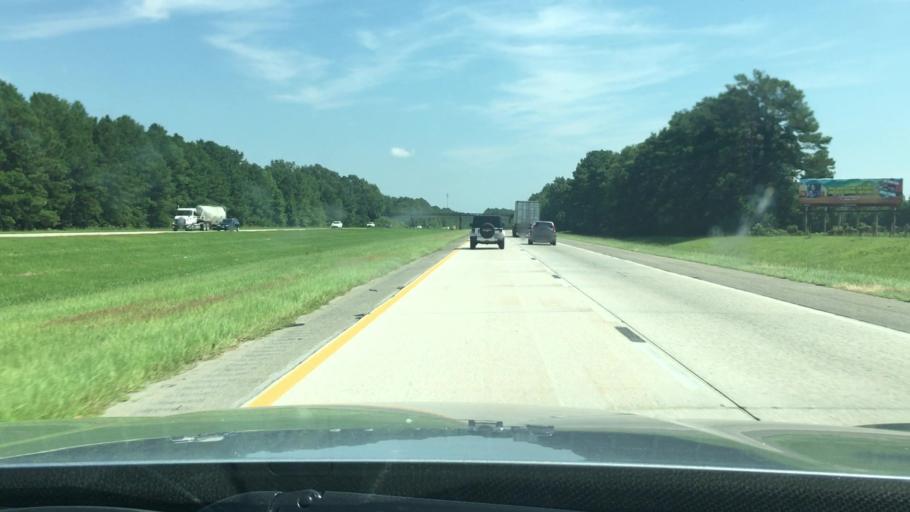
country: US
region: South Carolina
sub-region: Florence County
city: Timmonsville
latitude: 34.0480
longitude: -79.9774
